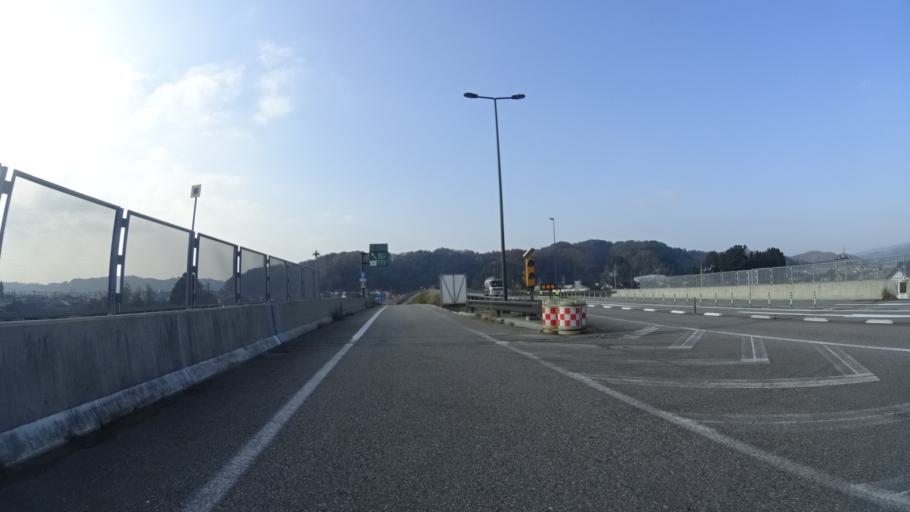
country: JP
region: Toyama
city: Himi
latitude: 36.8786
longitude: 136.9734
